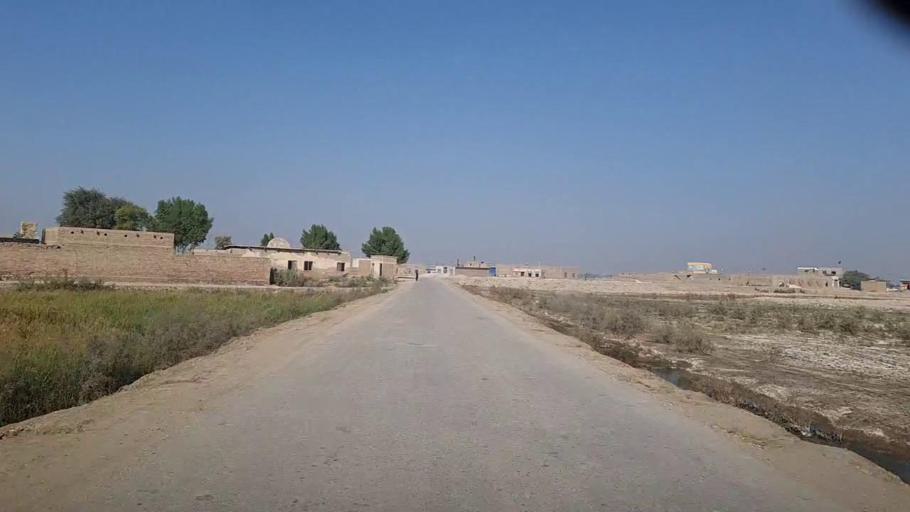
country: PK
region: Sindh
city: Tangwani
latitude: 28.2613
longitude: 68.9995
